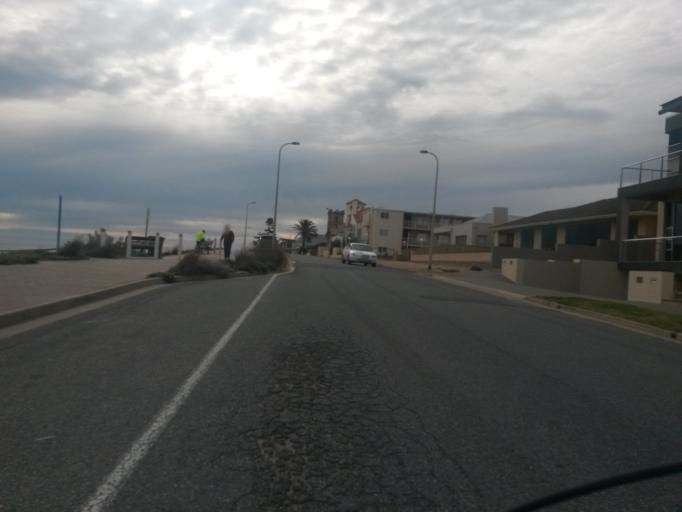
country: AU
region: South Australia
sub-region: Adelaide
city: Glenelg
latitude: -34.9692
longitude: 138.5105
